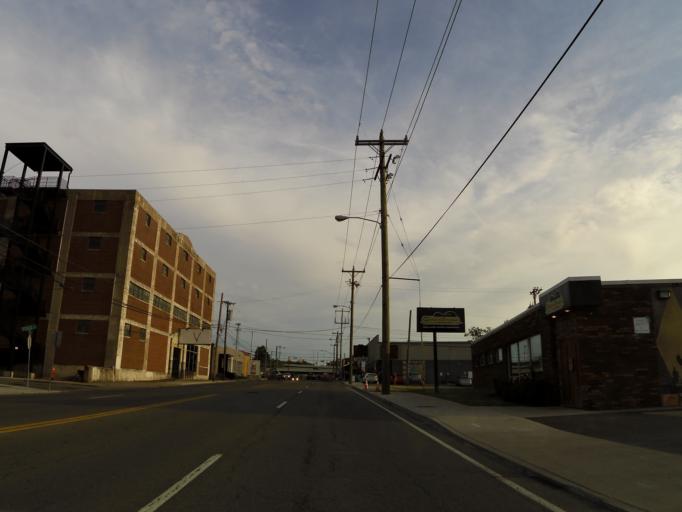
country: US
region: Tennessee
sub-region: Davidson County
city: Nashville
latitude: 36.1511
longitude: -86.7793
